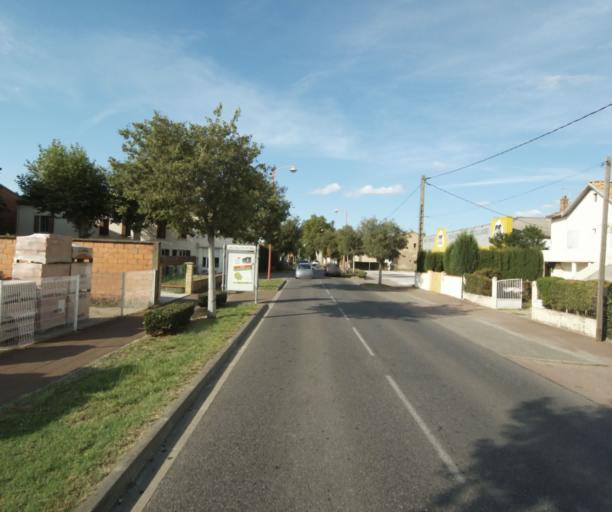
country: FR
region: Midi-Pyrenees
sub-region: Departement de la Haute-Garonne
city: Revel
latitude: 43.4645
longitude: 2.0080
